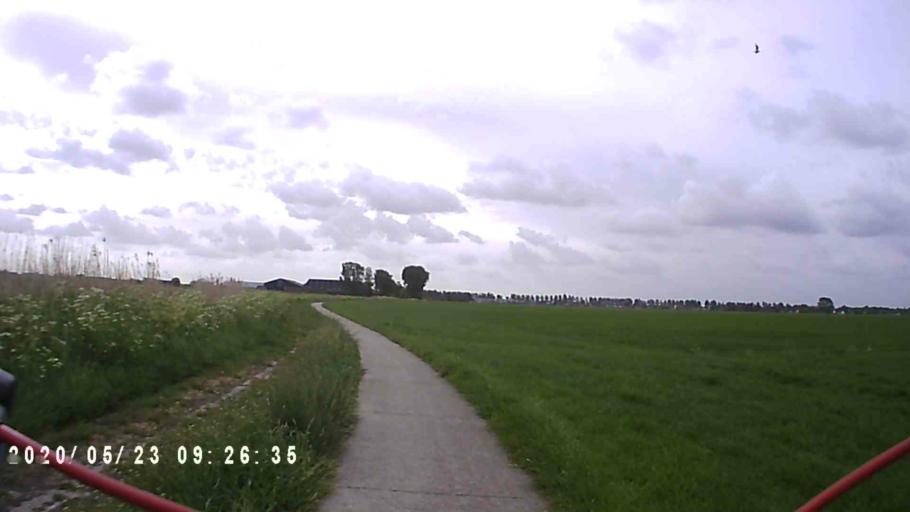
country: NL
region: Groningen
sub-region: Gemeente Bedum
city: Bedum
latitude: 53.2929
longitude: 6.6957
